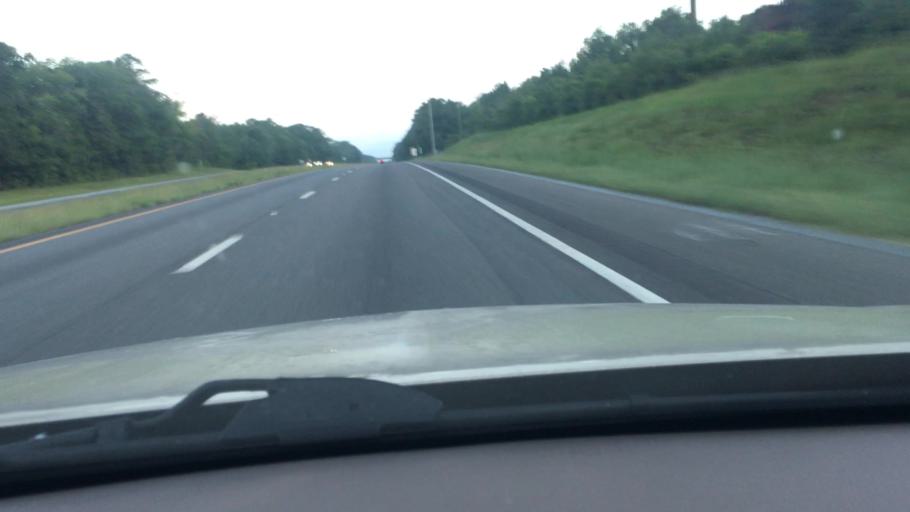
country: US
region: South Carolina
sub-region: Lexington County
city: Irmo
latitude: 34.1149
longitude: -81.1911
